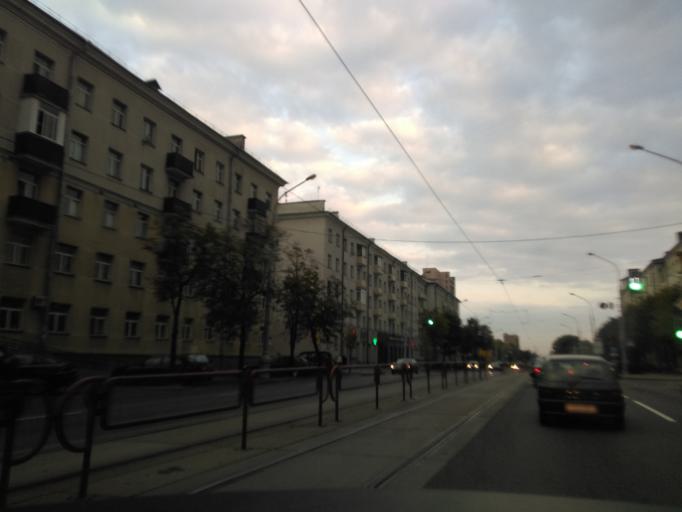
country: BY
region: Minsk
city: Minsk
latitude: 53.9002
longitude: 27.6030
